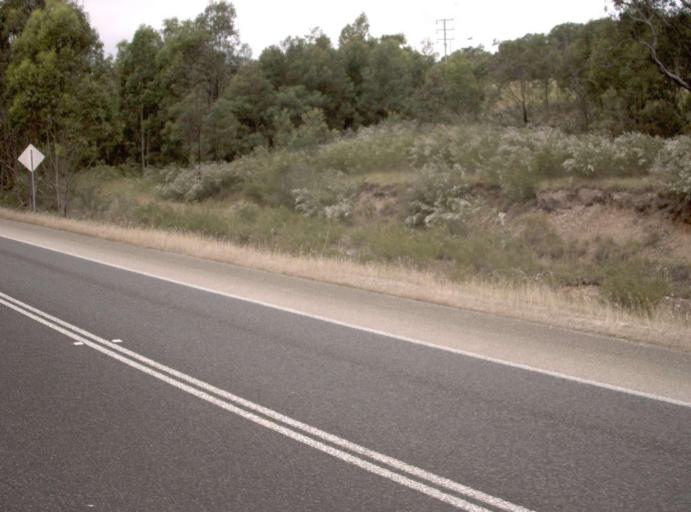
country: AU
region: Victoria
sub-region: East Gippsland
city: Lakes Entrance
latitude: -37.7207
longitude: 147.8509
